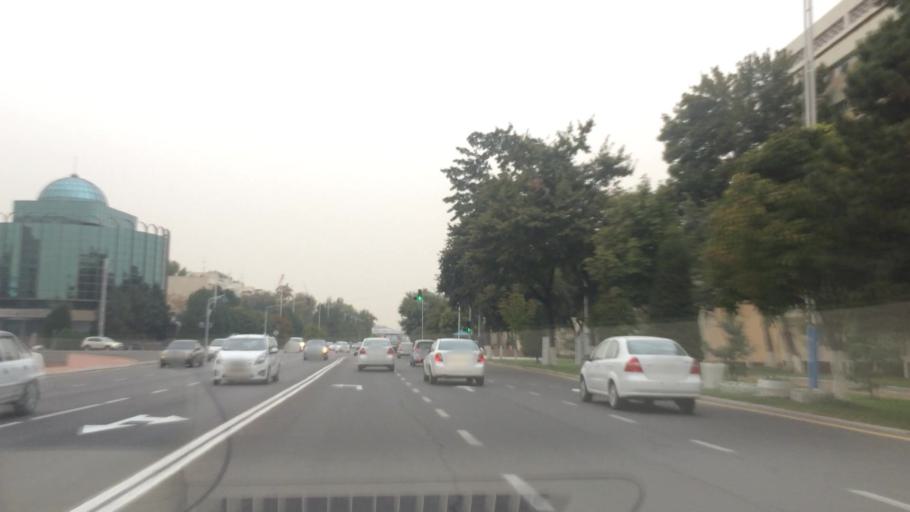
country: UZ
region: Toshkent Shahri
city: Tashkent
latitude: 41.3054
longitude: 69.2650
